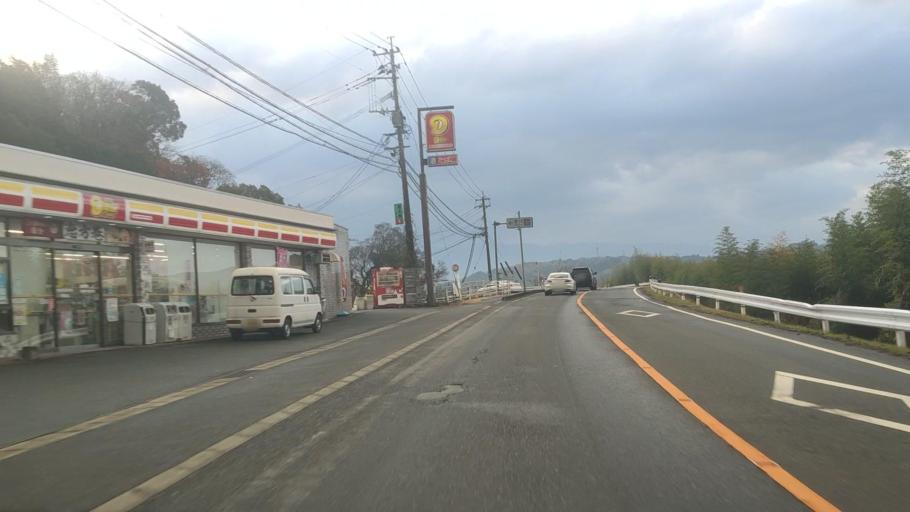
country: JP
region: Kumamoto
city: Uto
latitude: 32.6965
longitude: 130.7880
